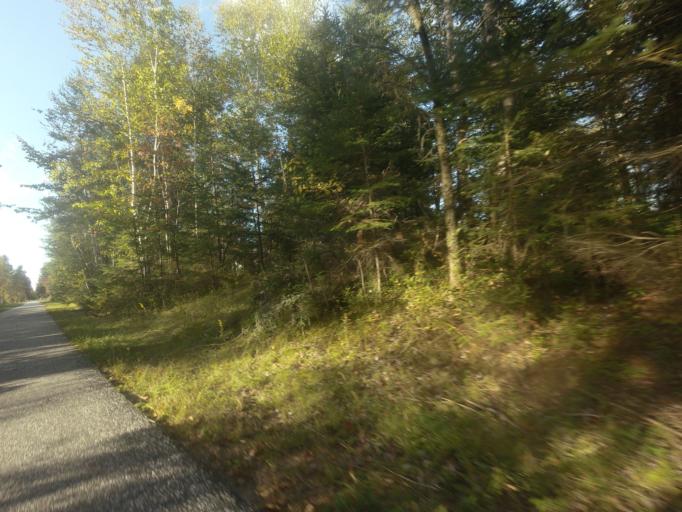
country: CA
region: Quebec
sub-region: Laurentides
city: Riviere-Rouge
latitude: 46.4186
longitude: -74.8761
